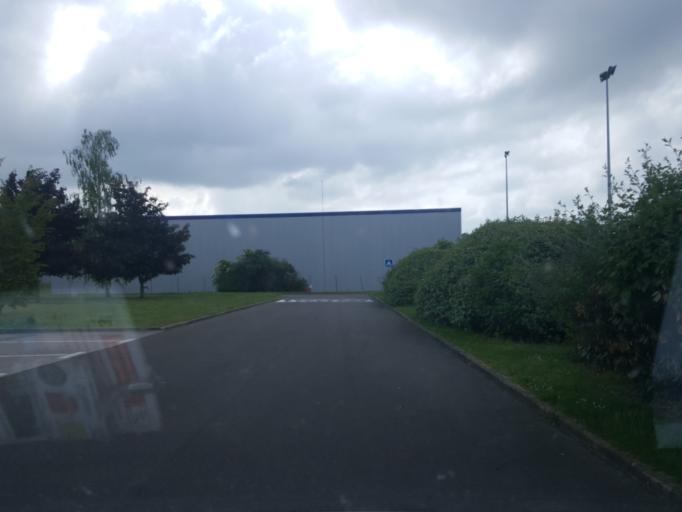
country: FR
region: Haute-Normandie
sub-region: Departement de l'Eure
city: Saint-Pierre-du-Vauvray
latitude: 49.1990
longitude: 1.2190
